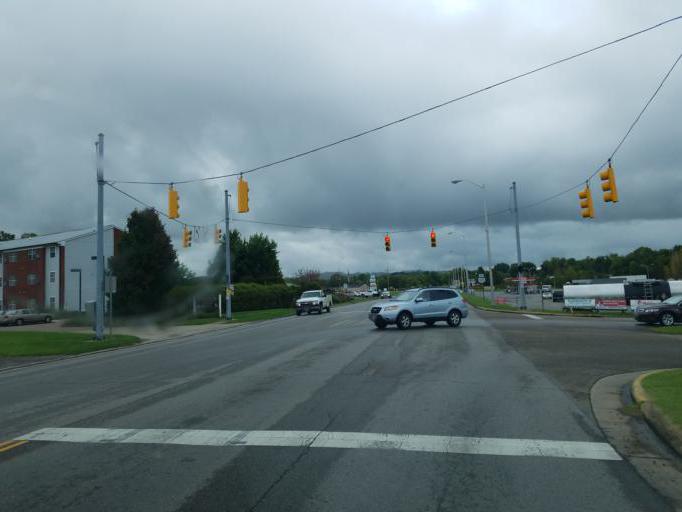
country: US
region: Ohio
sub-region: Scioto County
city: Wheelersburg
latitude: 38.7147
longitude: -82.8566
